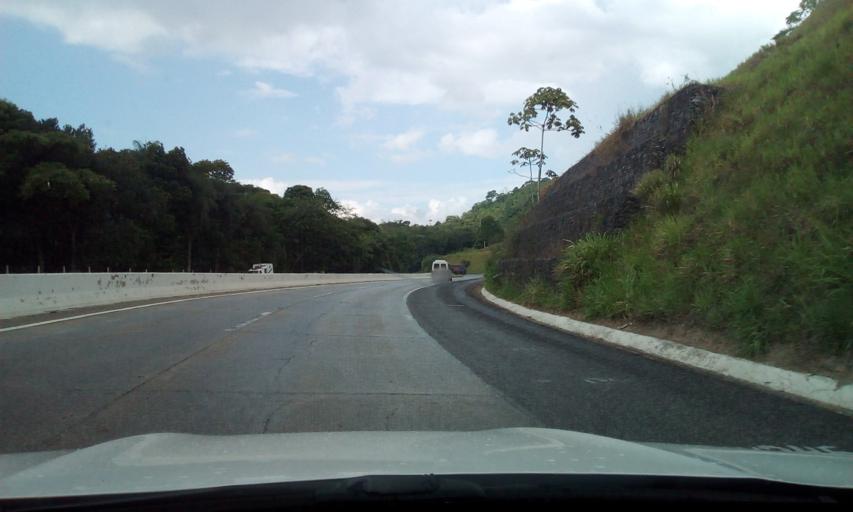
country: BR
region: Pernambuco
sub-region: Cabo De Santo Agostinho
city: Cabo
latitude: -8.3118
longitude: -35.1005
